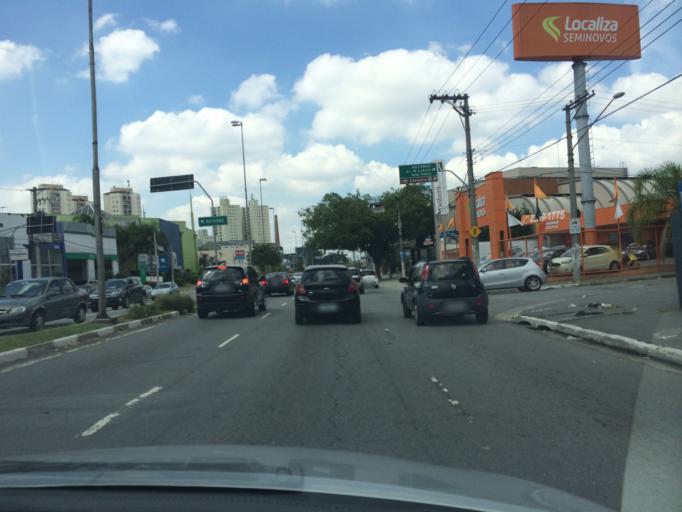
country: BR
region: Sao Paulo
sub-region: Guarulhos
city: Guarulhos
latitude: -23.4678
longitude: -46.5230
